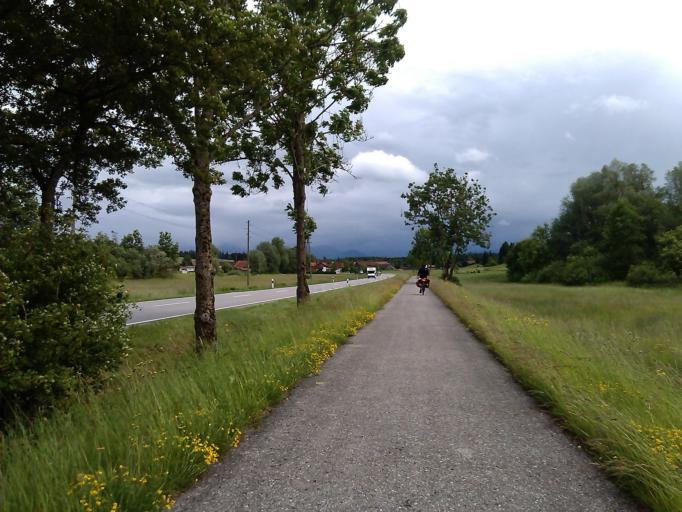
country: DE
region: Bavaria
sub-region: Swabia
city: Stotten am Auerberg
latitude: 47.7121
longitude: 10.6914
